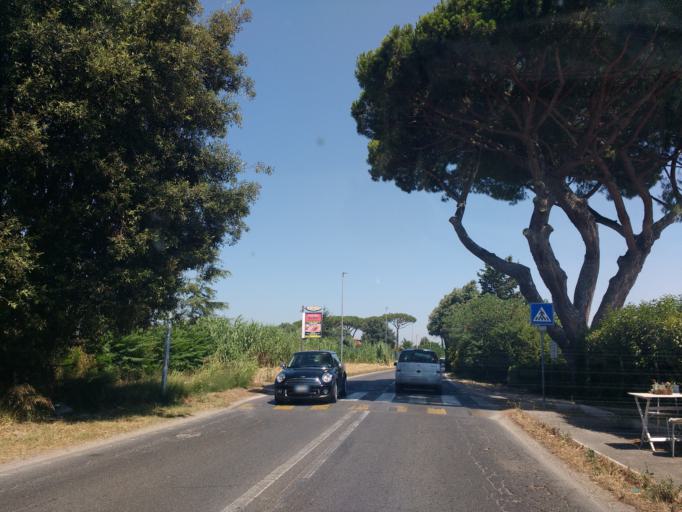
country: IT
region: Latium
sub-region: Citta metropolitana di Roma Capitale
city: Maccarese
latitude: 41.8706
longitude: 12.2086
